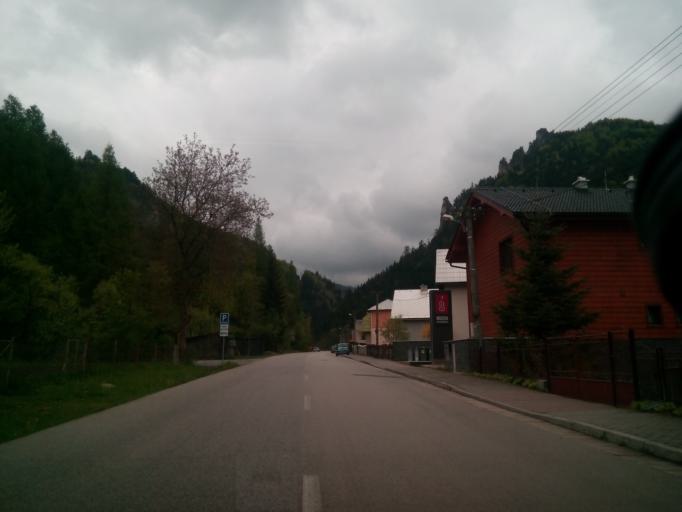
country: SK
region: Zilinsky
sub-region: Okres Zilina
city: Terchova
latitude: 49.2532
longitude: 19.0369
